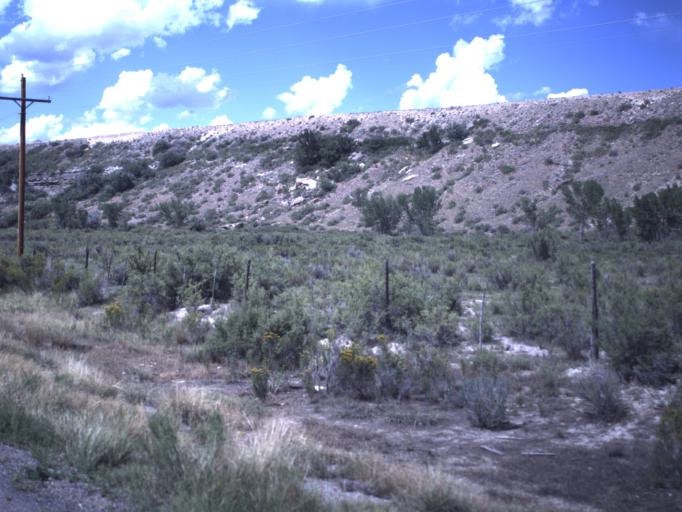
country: US
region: Utah
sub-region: Duchesne County
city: Duchesne
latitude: 40.1671
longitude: -110.4158
